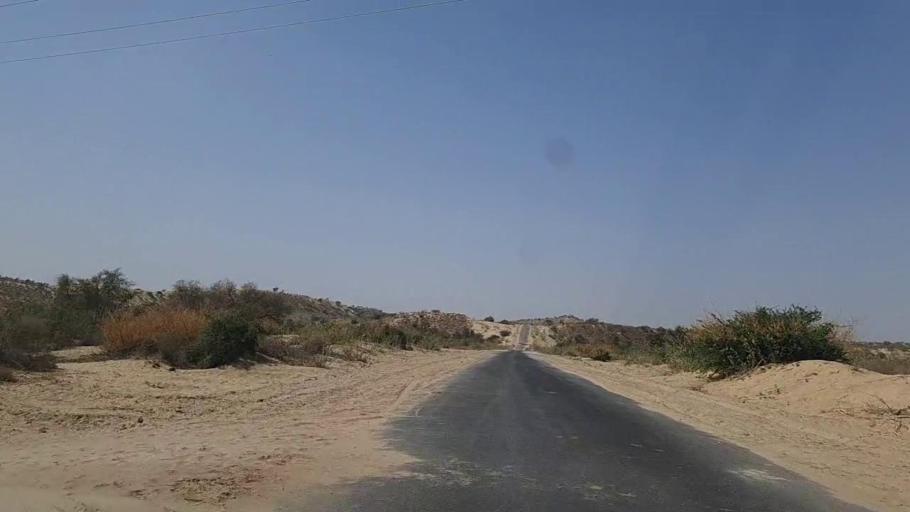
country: PK
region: Sindh
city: Diplo
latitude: 24.5763
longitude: 69.4889
